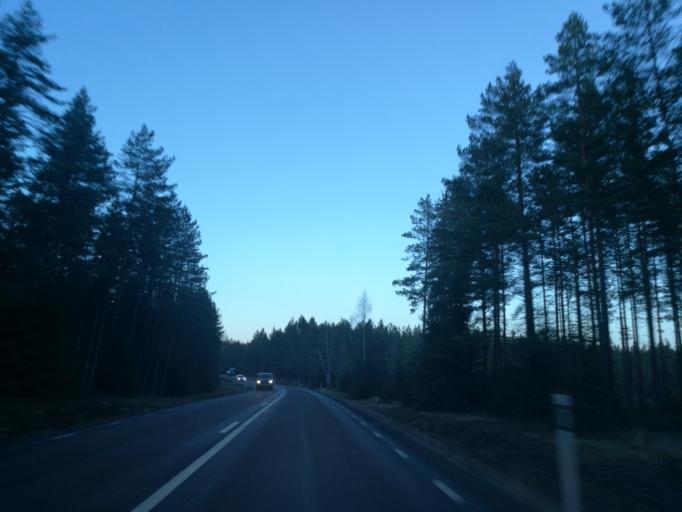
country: SE
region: Vaermland
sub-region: Eda Kommun
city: Charlottenberg
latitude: 59.9009
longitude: 12.2795
